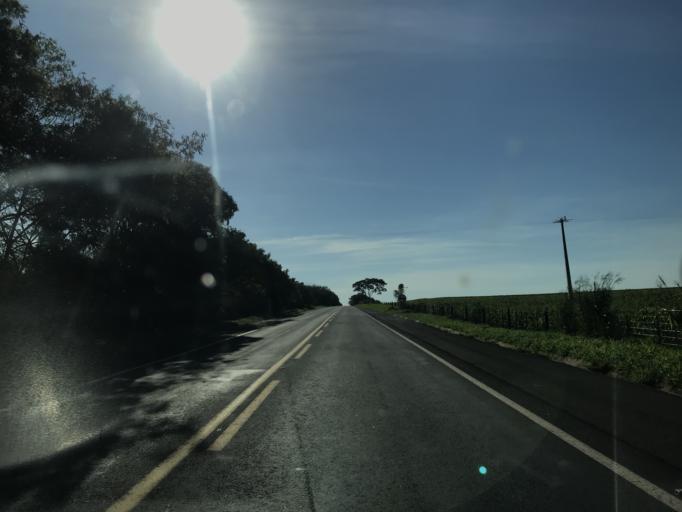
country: BR
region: Parana
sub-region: Ipora
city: Ipora
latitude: -23.9626
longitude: -53.6210
